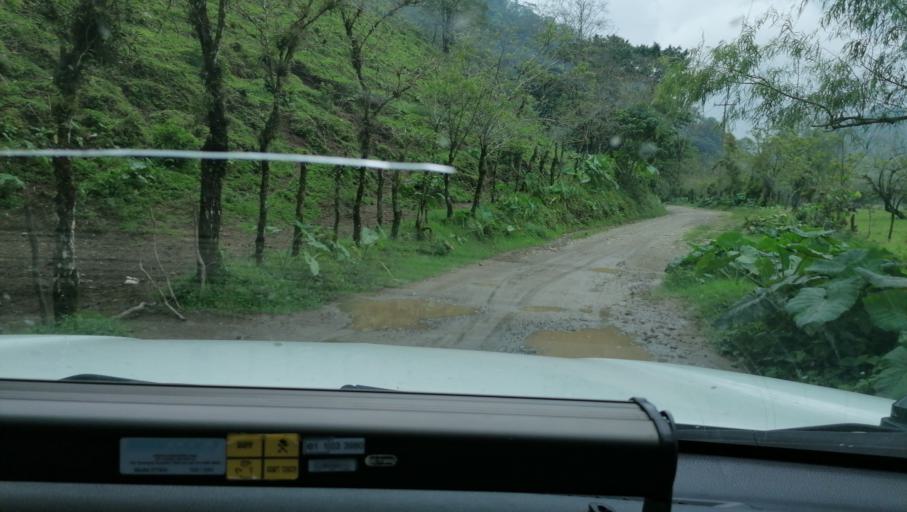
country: MX
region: Chiapas
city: Ixtacomitan
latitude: 17.3578
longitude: -93.1681
